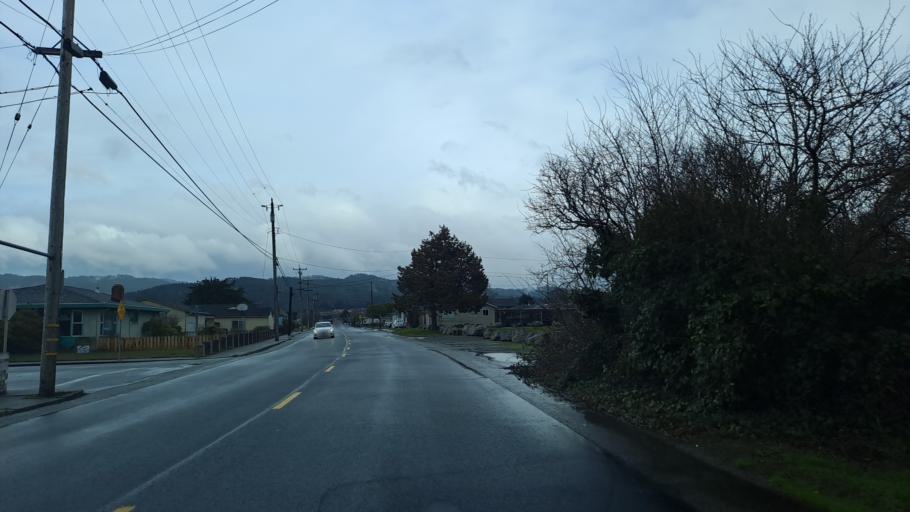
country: US
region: California
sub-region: Humboldt County
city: Fortuna
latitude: 40.5886
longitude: -124.1517
